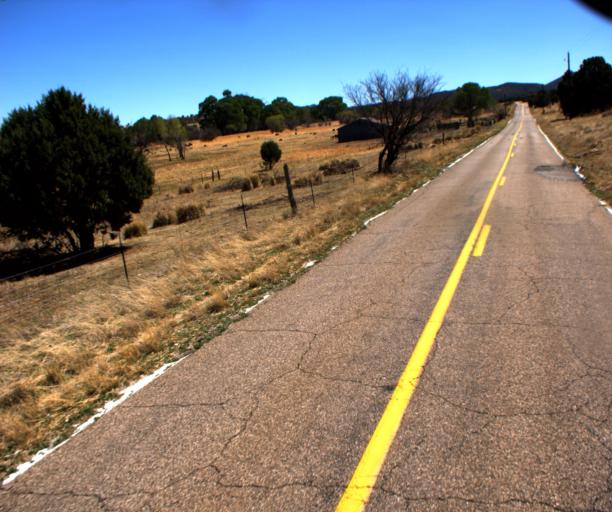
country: US
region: Arizona
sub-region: Cochise County
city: Huachuca City
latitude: 31.5530
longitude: -110.5290
